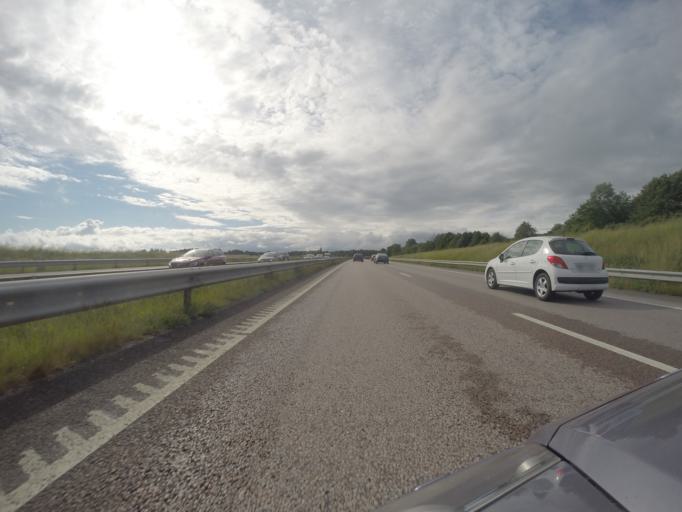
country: SE
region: Skane
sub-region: Kavlinge Kommun
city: Loddekopinge
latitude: 55.7525
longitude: 13.0059
